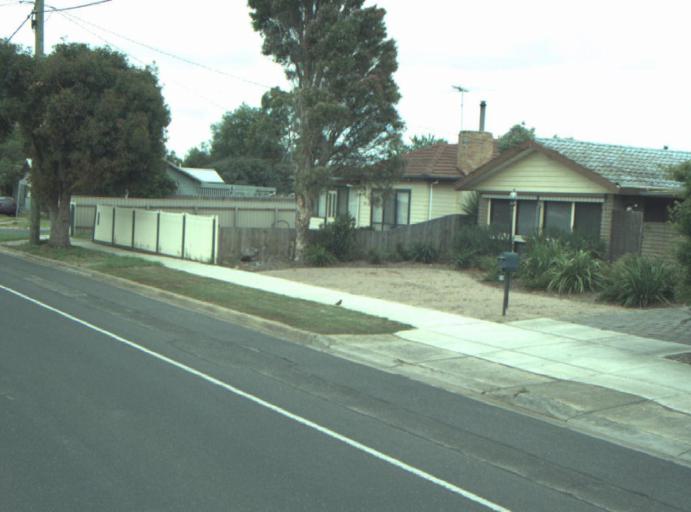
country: AU
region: Victoria
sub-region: Greater Geelong
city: Lara
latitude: -38.0307
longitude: 144.4129
